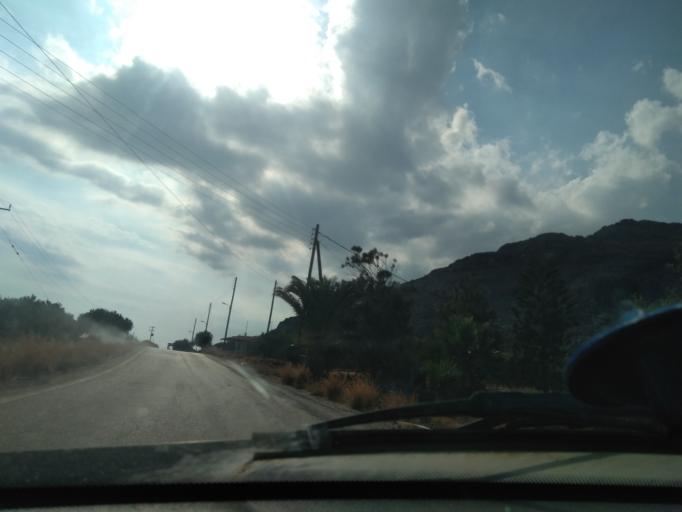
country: GR
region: Crete
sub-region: Nomos Lasithiou
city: Makry-Gialos
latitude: 35.0187
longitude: 26.0277
